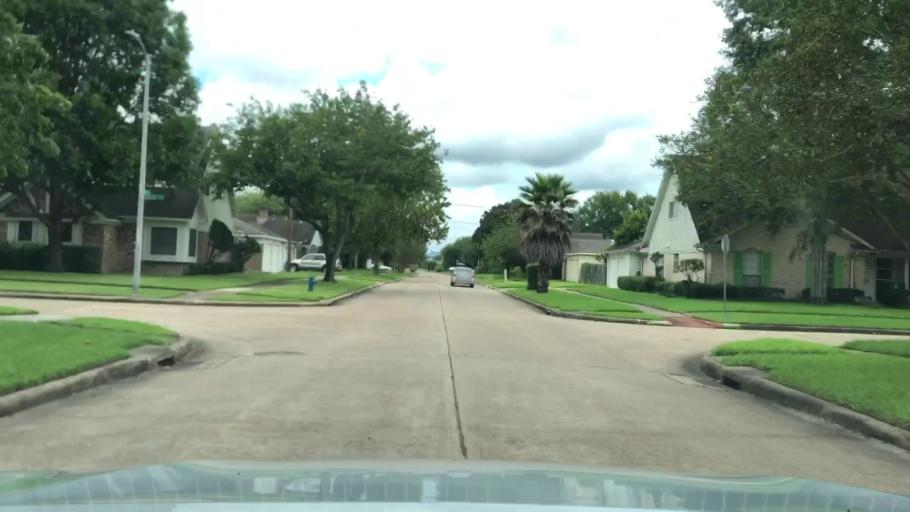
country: US
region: Texas
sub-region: Fort Bend County
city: Meadows Place
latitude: 29.7011
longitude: -95.5471
